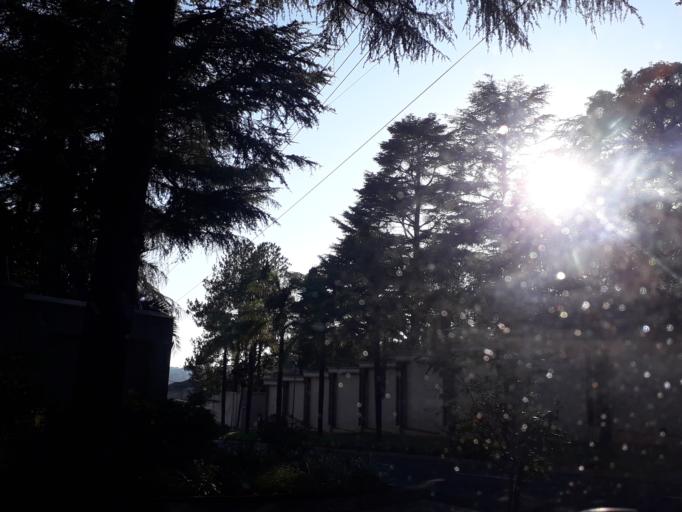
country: ZA
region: Gauteng
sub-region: City of Johannesburg Metropolitan Municipality
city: Modderfontein
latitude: -26.0861
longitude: 28.0621
